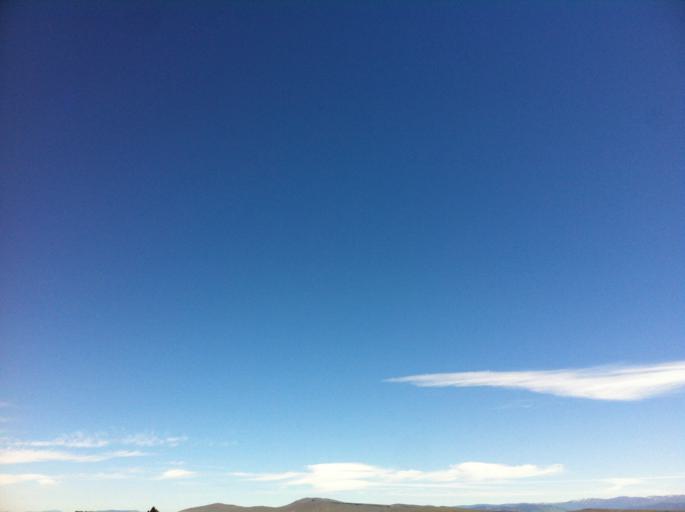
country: US
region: Oregon
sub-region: Baker County
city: Baker City
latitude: 44.8325
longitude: -117.8133
